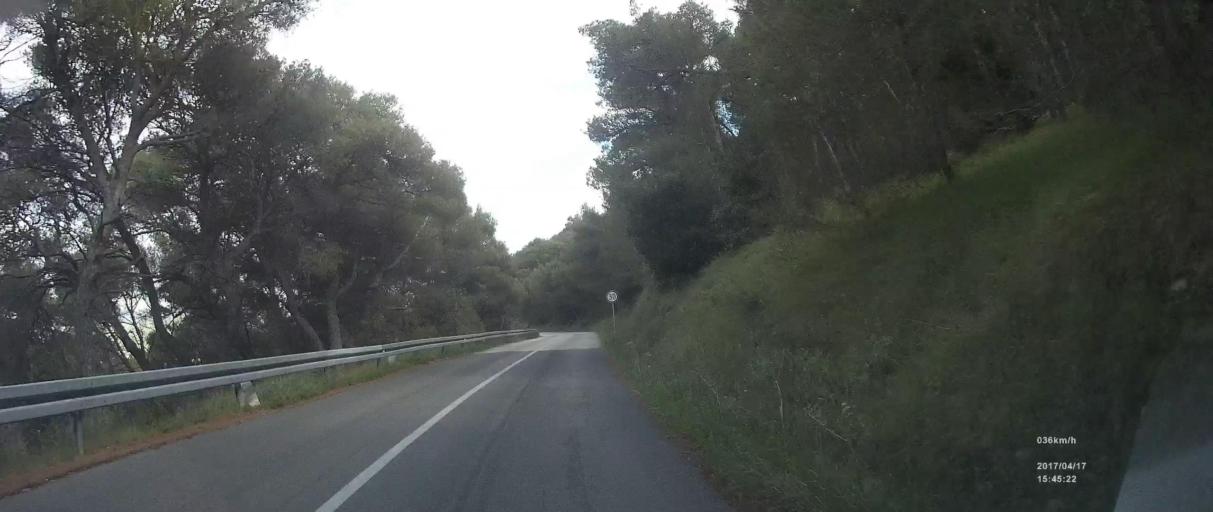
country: HR
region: Sibensko-Kniniska
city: Primosten
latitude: 43.6273
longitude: 15.9616
